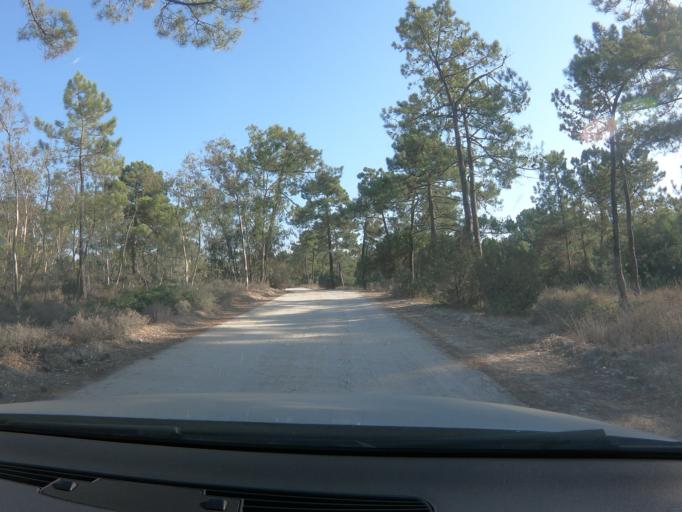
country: PT
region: Setubal
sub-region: Setubal
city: Setubal
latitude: 38.4732
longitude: -8.8789
